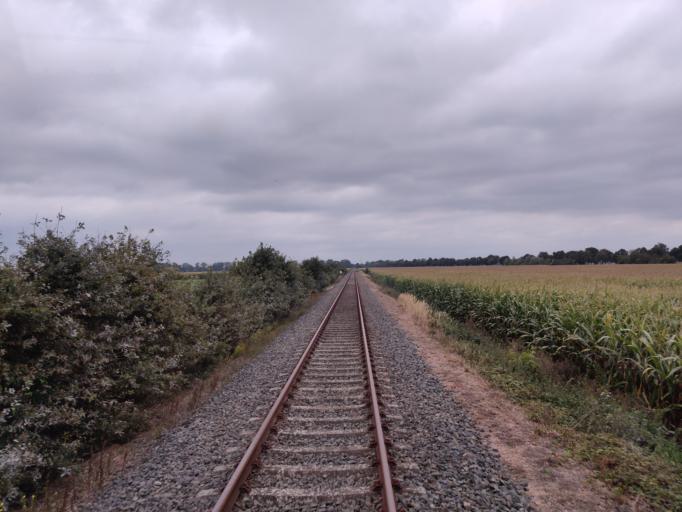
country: DE
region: Lower Saxony
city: Vollersode
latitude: 53.2995
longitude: 8.9698
